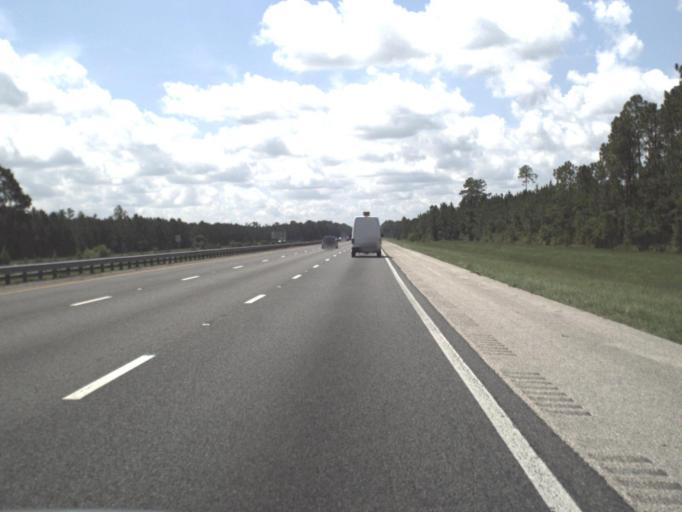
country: US
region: Florida
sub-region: Saint Johns County
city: Saint Augustine Shores
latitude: 29.8082
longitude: -81.3709
